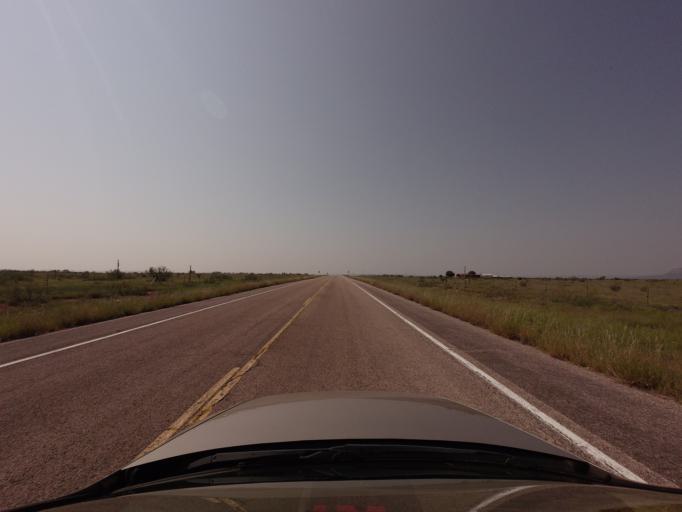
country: US
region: New Mexico
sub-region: Quay County
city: Tucumcari
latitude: 34.9570
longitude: -103.7576
